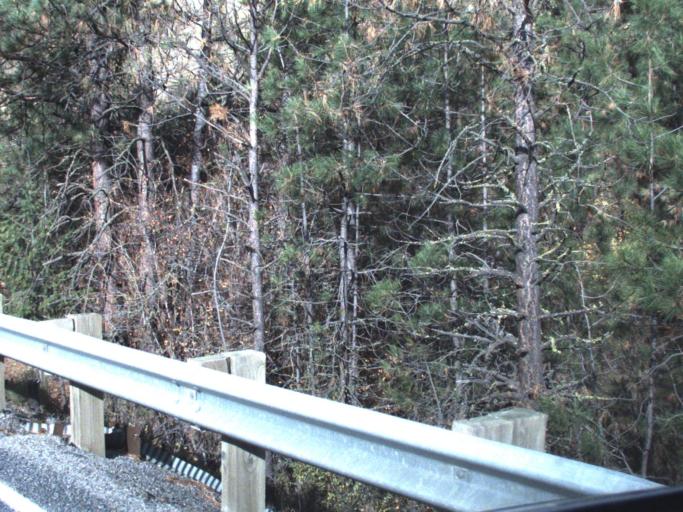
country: US
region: Washington
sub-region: Stevens County
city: Kettle Falls
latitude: 48.3243
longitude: -118.1519
